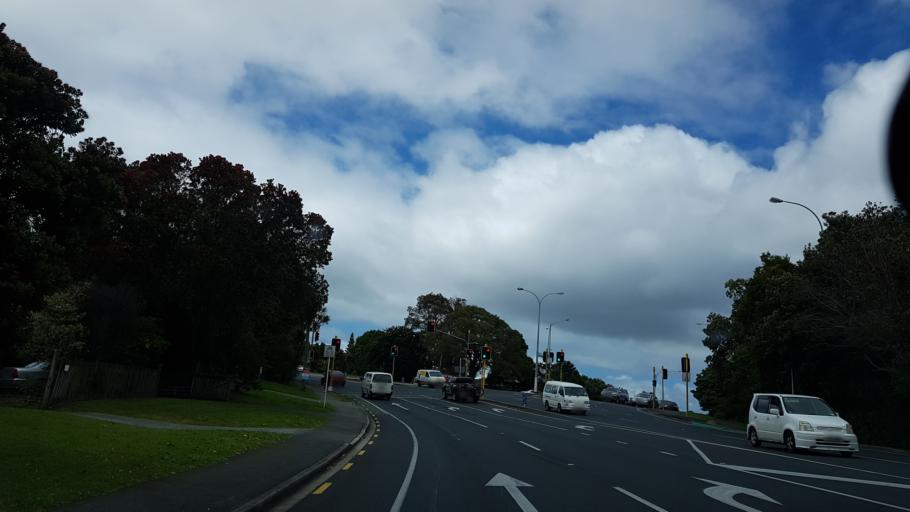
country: NZ
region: Auckland
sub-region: Auckland
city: Rothesay Bay
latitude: -36.7441
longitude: 174.7396
